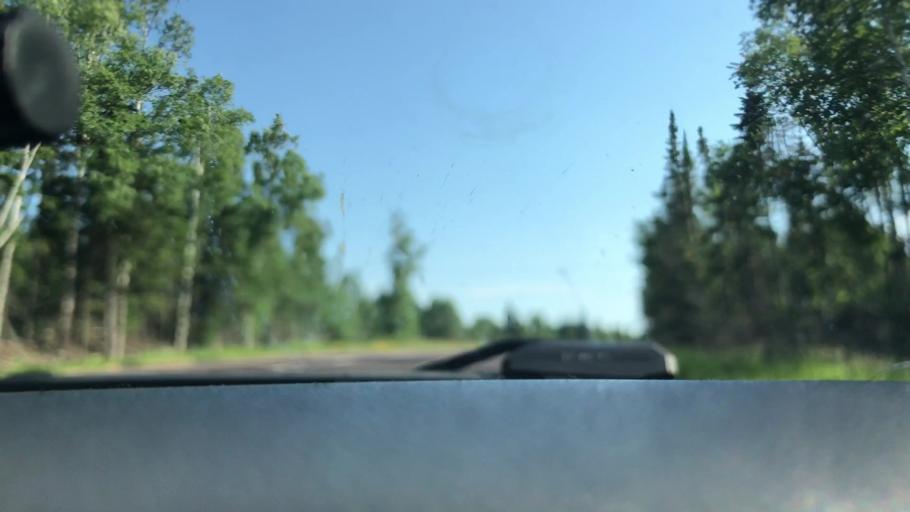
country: US
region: Minnesota
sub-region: Cook County
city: Grand Marais
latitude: 47.8353
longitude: -89.9736
